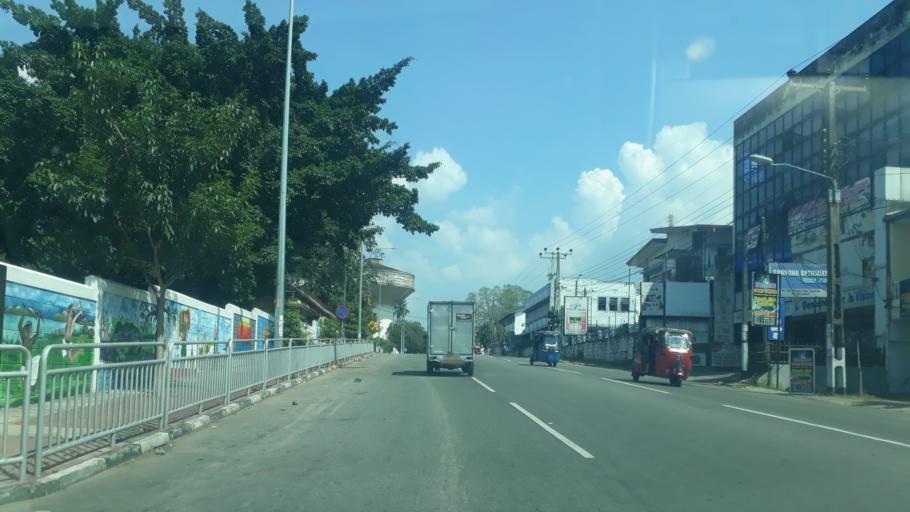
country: LK
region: Western
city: Gampaha
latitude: 7.0908
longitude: 80.0007
